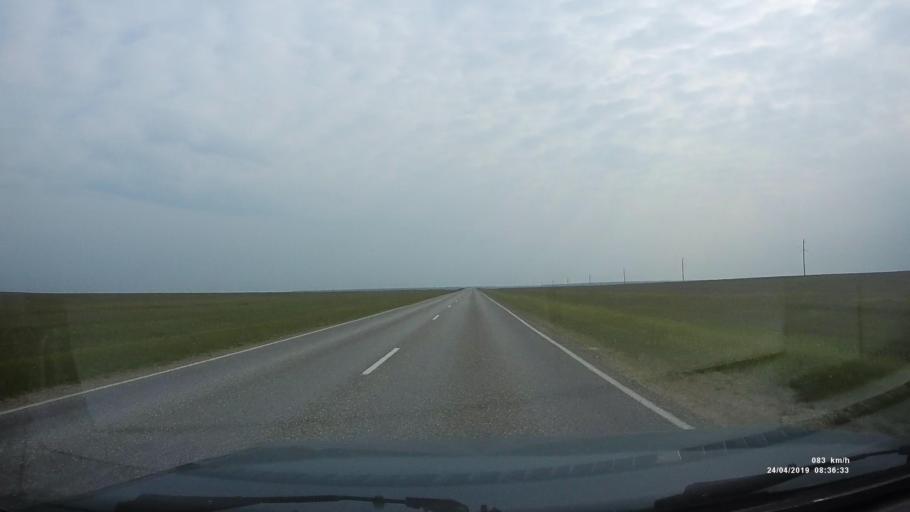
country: RU
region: Kalmykiya
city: Arshan'
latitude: 46.2053
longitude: 43.9363
